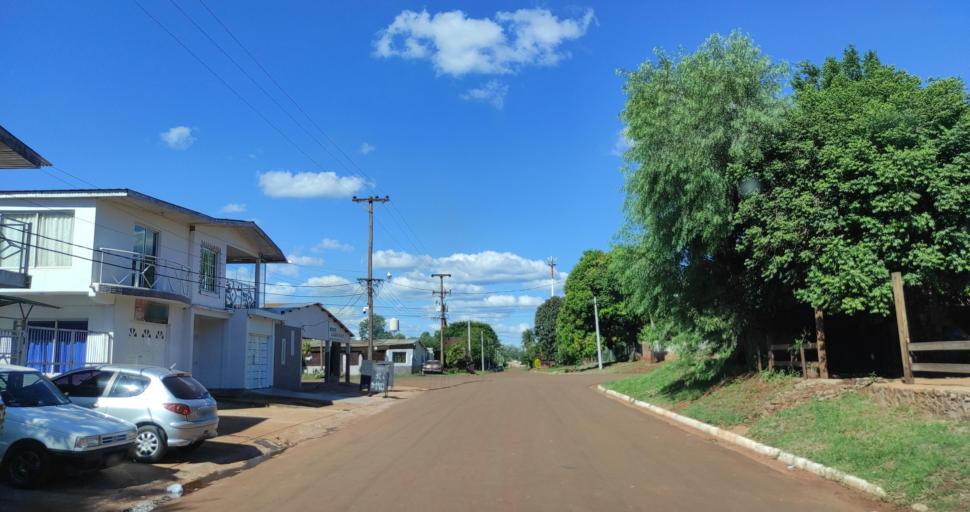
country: AR
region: Misiones
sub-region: Departamento de Candelaria
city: Candelaria
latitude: -27.4600
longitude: -55.7389
